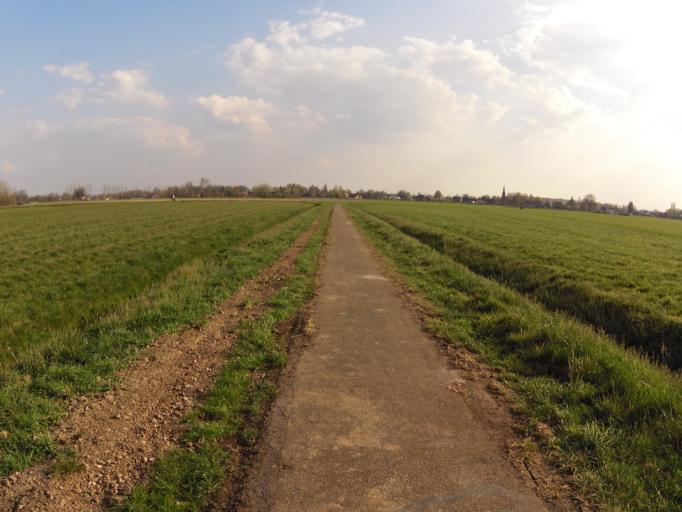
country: NL
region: North Brabant
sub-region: Gemeente Grave
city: Grave
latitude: 51.7801
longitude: 5.7460
